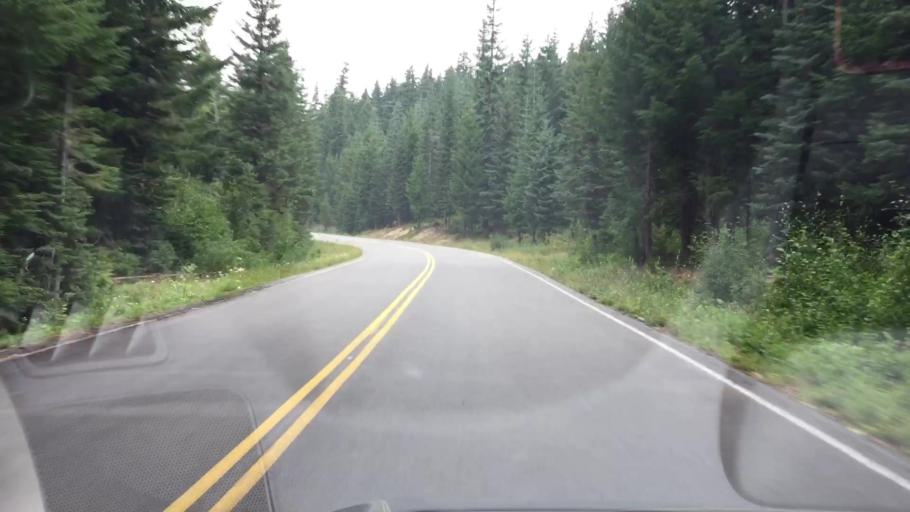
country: US
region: Washington
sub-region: Klickitat County
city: White Salmon
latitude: 46.1721
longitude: -121.6305
